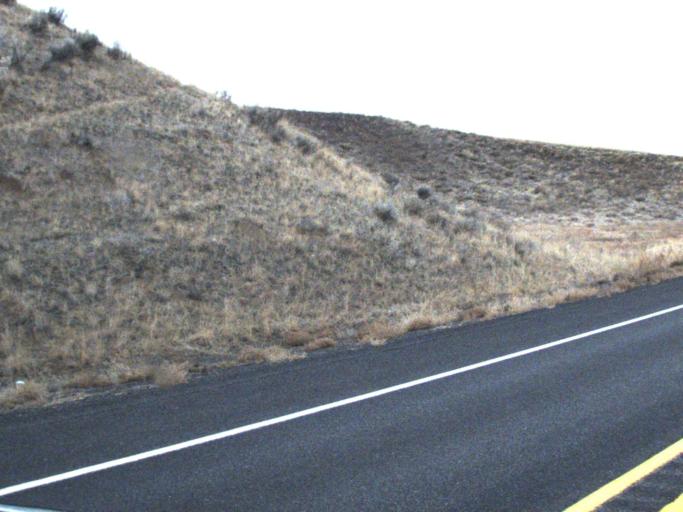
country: US
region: Washington
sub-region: Garfield County
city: Pomeroy
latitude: 46.8135
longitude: -117.8113
